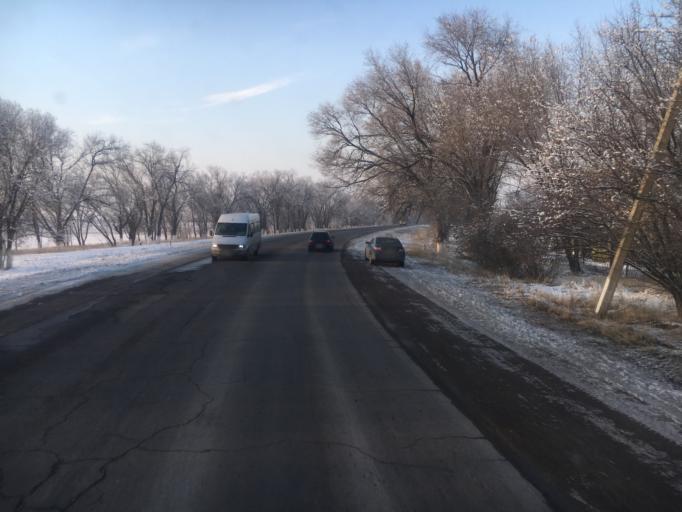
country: KZ
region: Almaty Oblysy
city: Burunday
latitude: 43.3080
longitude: 76.6670
